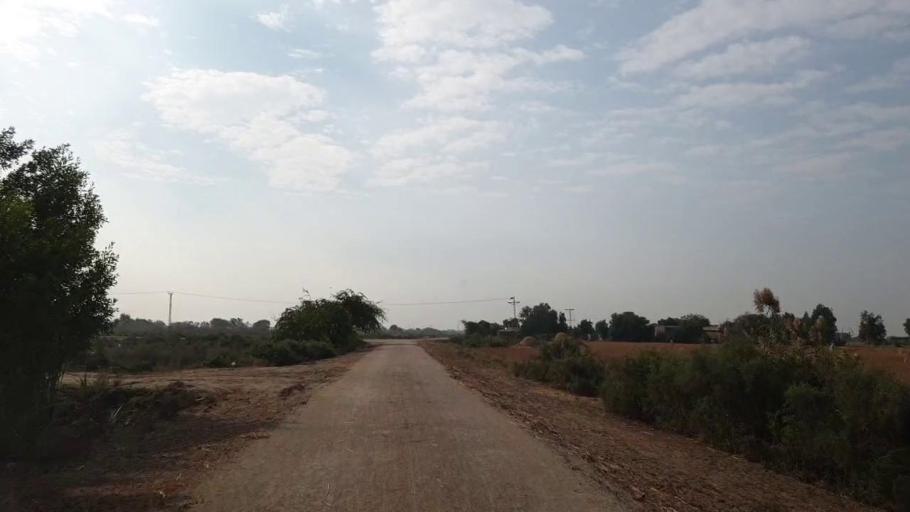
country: PK
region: Sindh
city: Tando Muhammad Khan
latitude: 25.0250
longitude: 68.4504
